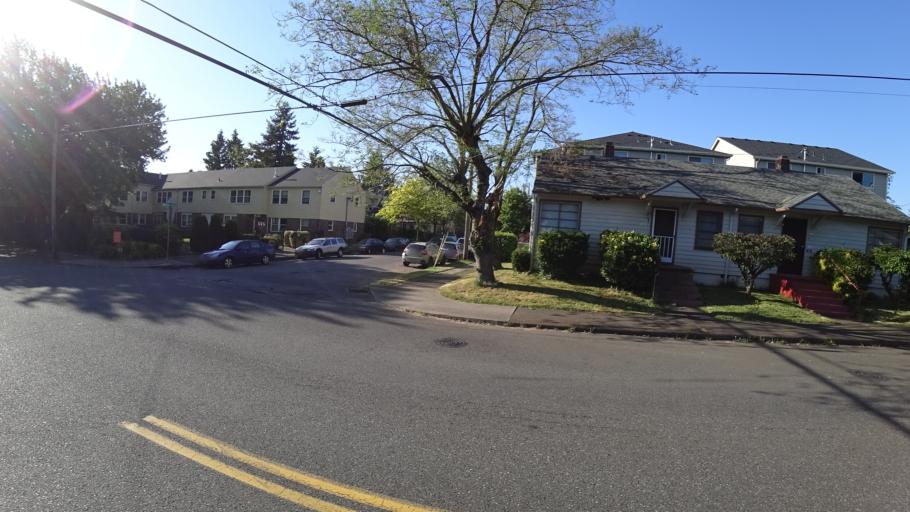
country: US
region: Oregon
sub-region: Multnomah County
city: Portland
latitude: 45.5590
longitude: -122.6809
